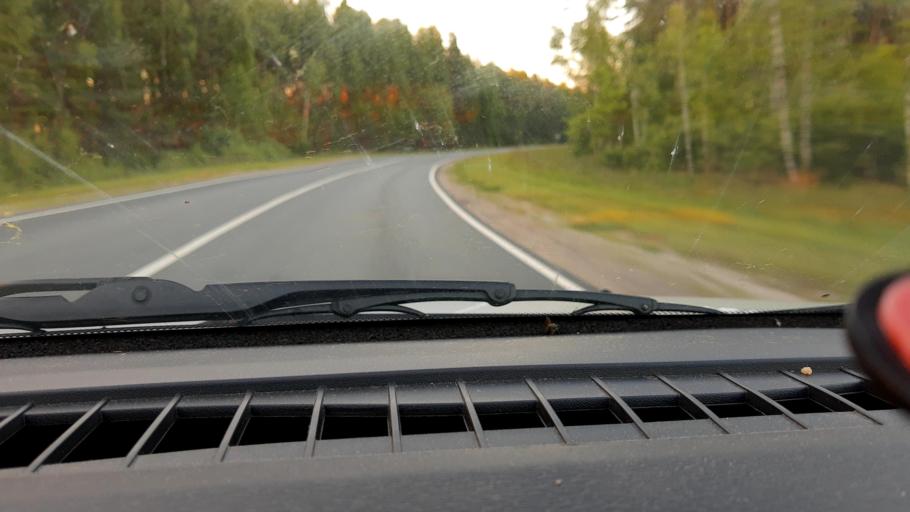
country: RU
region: Nizjnij Novgorod
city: Krasnyye Baki
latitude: 57.1765
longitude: 45.3277
